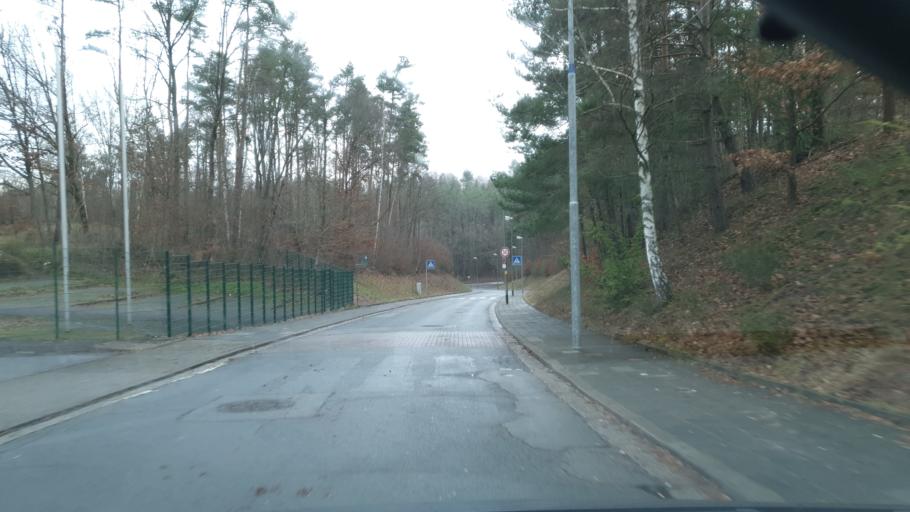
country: DE
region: Rheinland-Pfalz
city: Kaiserslautern
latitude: 49.4262
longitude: 7.7735
